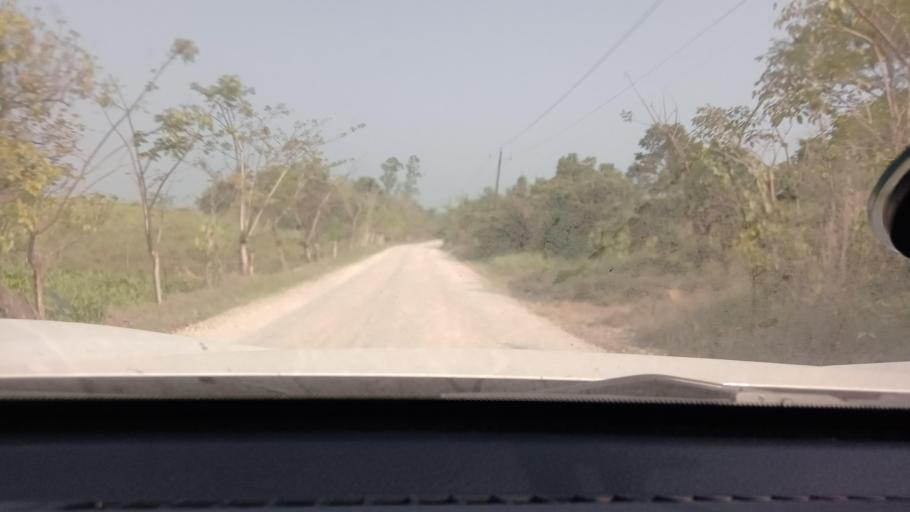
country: MX
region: Tabasco
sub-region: Huimanguillo
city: Francisco Rueda
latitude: 17.6201
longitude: -93.9421
